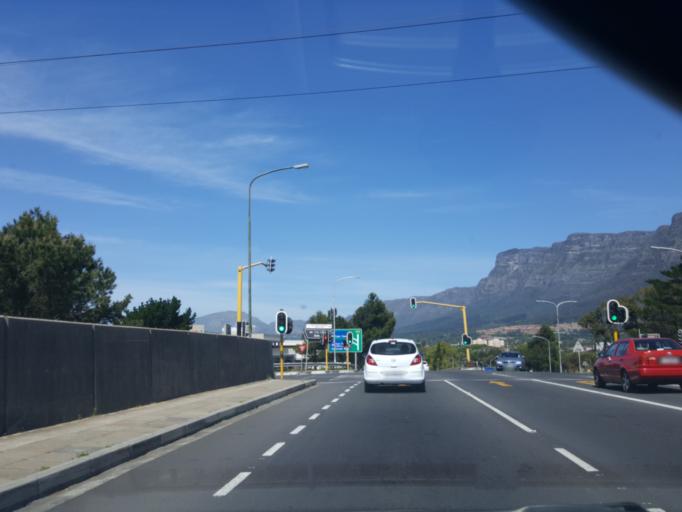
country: ZA
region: Western Cape
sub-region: City of Cape Town
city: Rosebank
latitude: -33.9449
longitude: 18.4918
